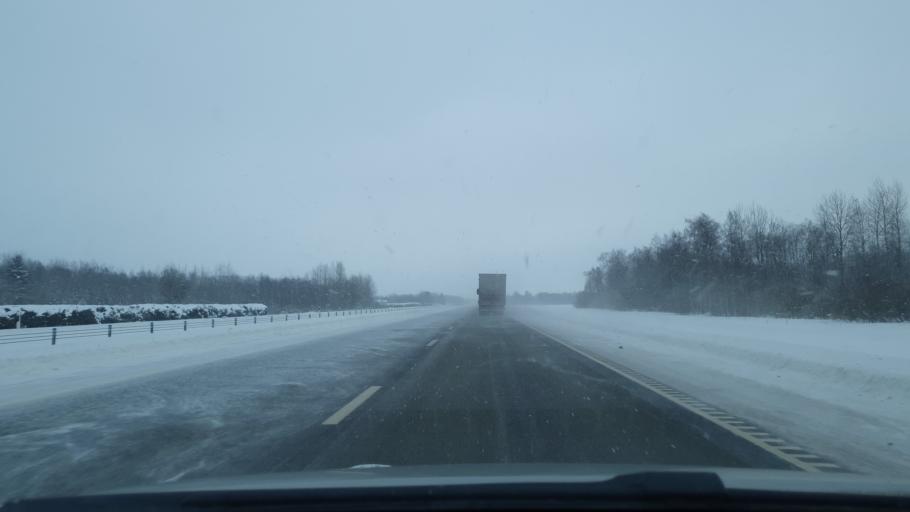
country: EE
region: Harju
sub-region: Anija vald
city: Kehra
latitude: 59.4423
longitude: 25.3182
